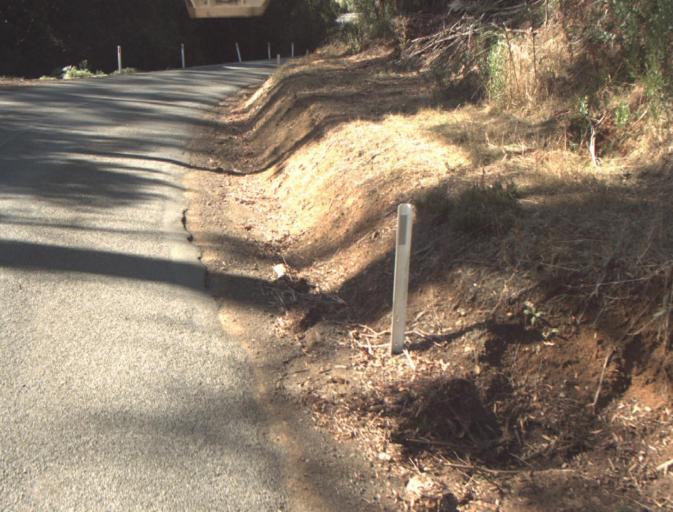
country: AU
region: Tasmania
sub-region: Launceston
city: Mayfield
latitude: -41.2969
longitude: 147.2010
